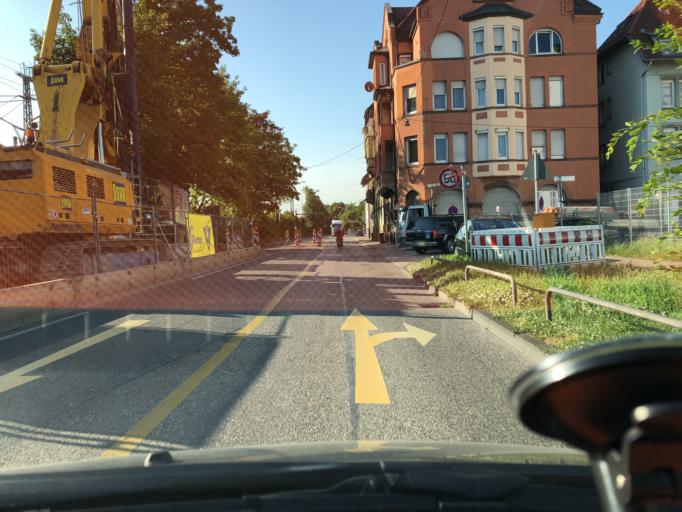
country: DE
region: Baden-Wuerttemberg
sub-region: Regierungsbezirk Stuttgart
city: Stuttgart-Ost
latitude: 48.7833
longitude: 9.2472
